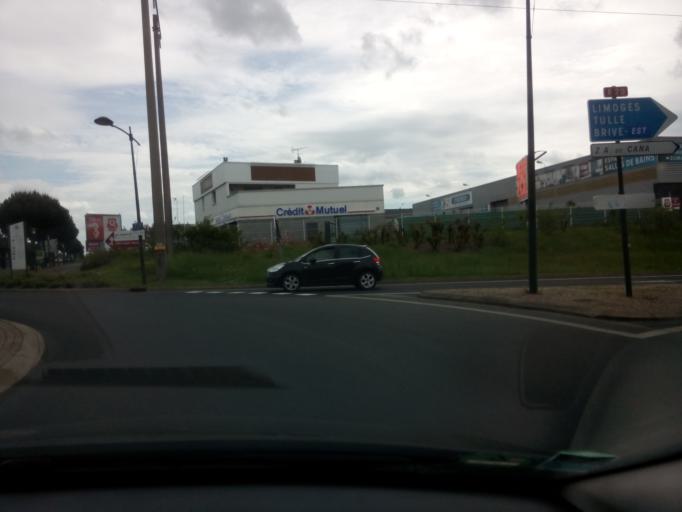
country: FR
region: Limousin
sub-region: Departement de la Correze
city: Saint-Pantaleon-de-Larche
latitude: 45.1473
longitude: 1.4863
